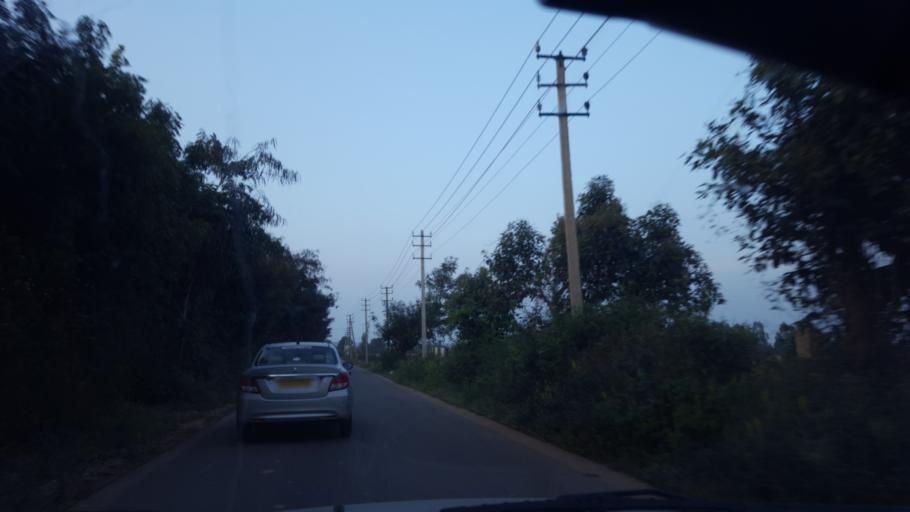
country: IN
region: Karnataka
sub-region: Bangalore Rural
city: Hoskote
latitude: 13.0783
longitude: 77.7040
